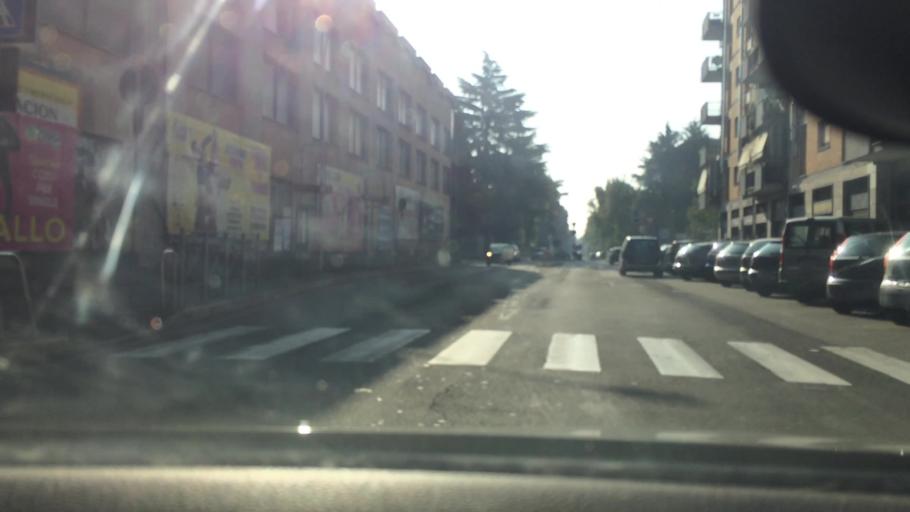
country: IT
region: Lombardy
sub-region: Citta metropolitana di Milano
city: Cerro Maggiore
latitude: 45.5971
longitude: 8.9549
